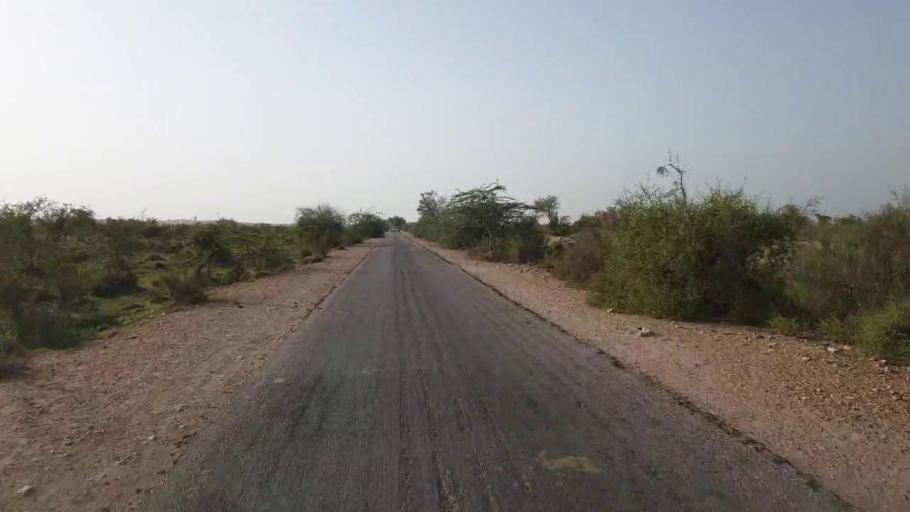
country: PK
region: Sindh
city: Jam Sahib
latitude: 26.4564
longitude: 68.8603
